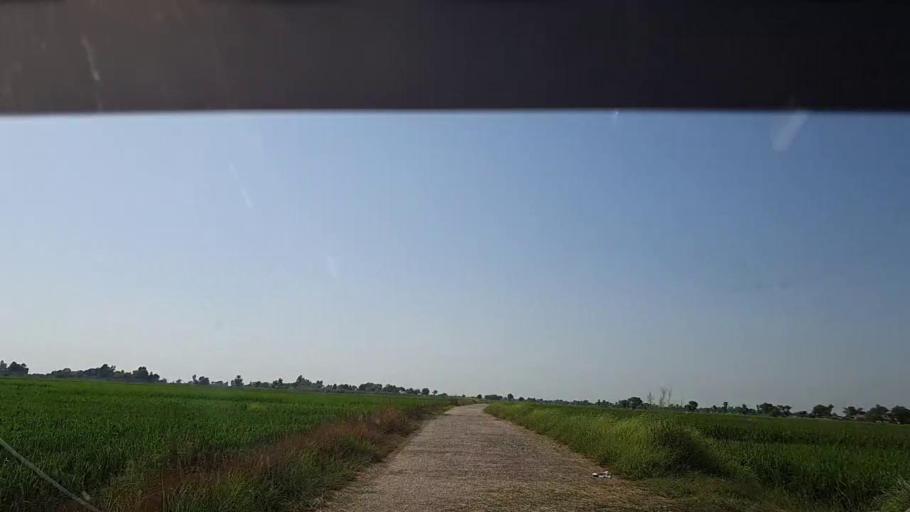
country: PK
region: Sindh
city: Ghauspur
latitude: 28.1787
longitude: 69.0346
